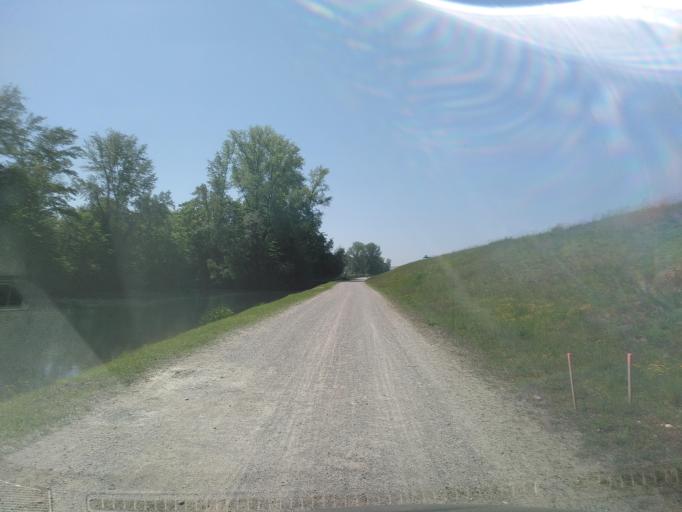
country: FR
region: Alsace
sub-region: Departement du Haut-Rhin
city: Kunheim
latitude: 48.0951
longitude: 7.5788
